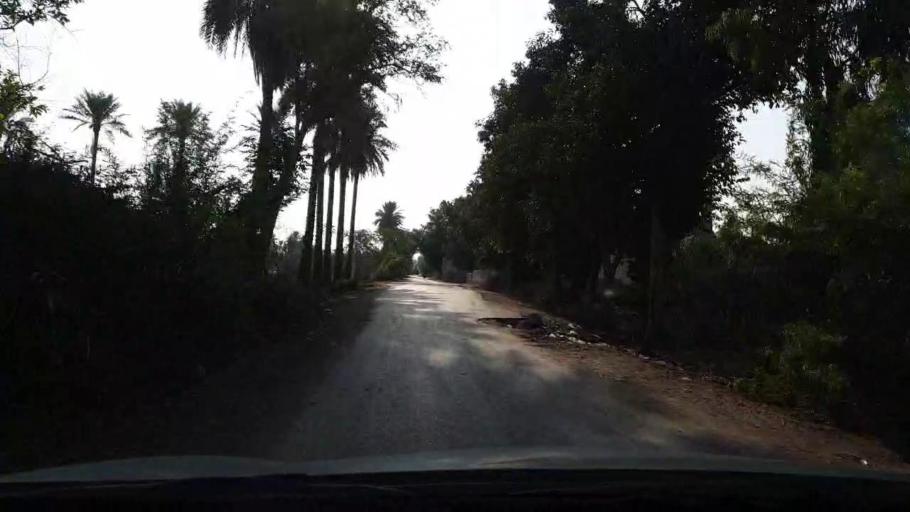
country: PK
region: Sindh
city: Larkana
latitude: 27.5513
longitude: 68.2337
